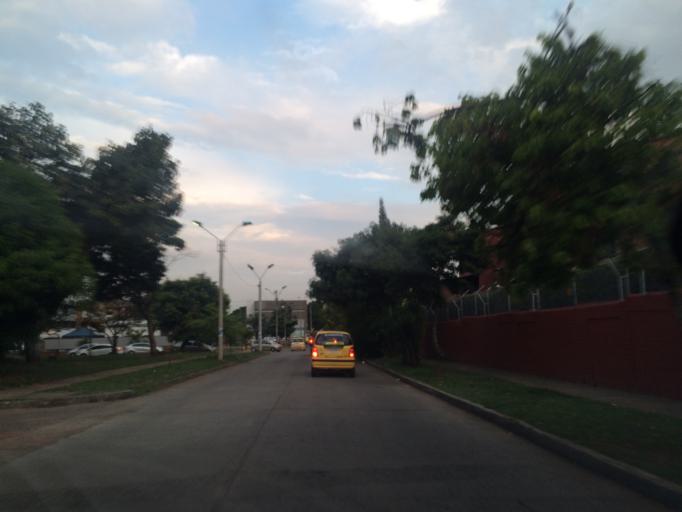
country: CO
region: Valle del Cauca
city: Cali
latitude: 3.4131
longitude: -76.5394
